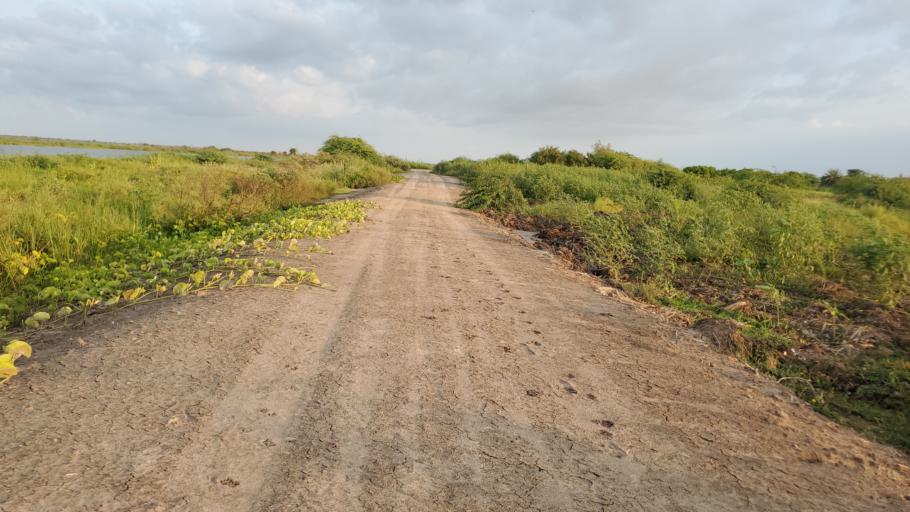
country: SN
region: Saint-Louis
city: Saint-Louis
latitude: 16.0173
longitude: -16.4015
